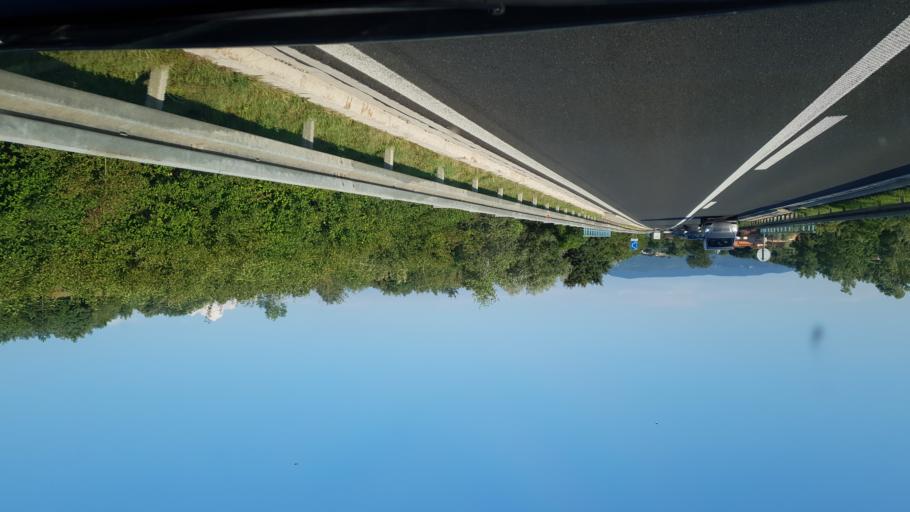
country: HR
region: Istarska
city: Pazin
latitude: 45.3000
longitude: 14.0494
